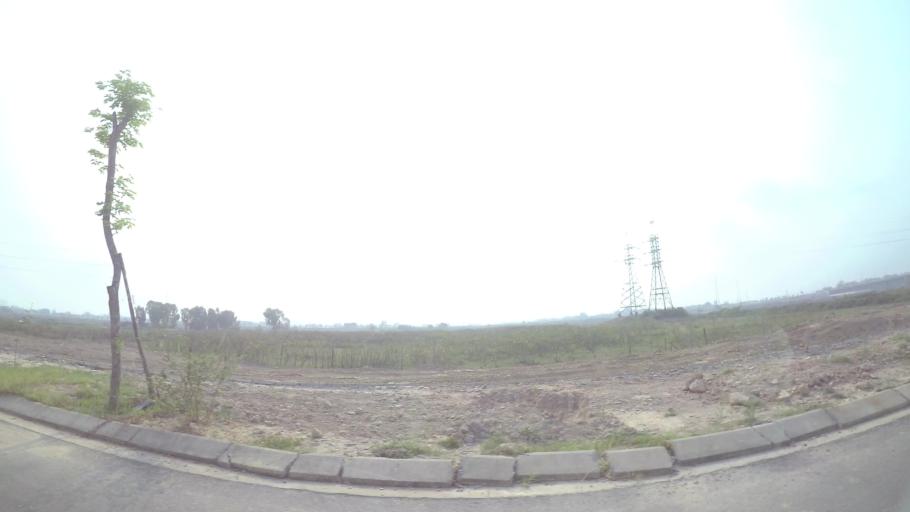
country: VN
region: Da Nang
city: Ngu Hanh Son
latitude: 16.0058
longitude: 108.2296
